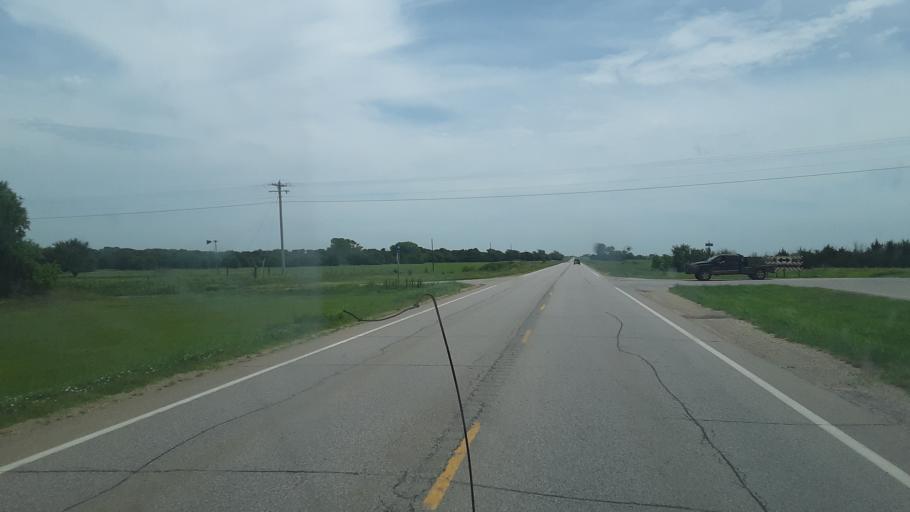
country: US
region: Kansas
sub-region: Butler County
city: El Dorado
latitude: 37.8105
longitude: -96.7349
